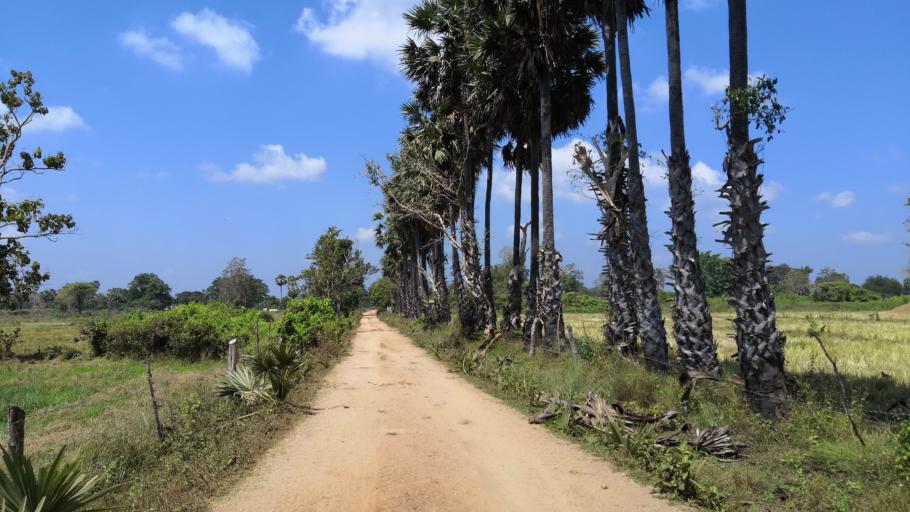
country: LK
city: Padaviya Divisional Secretariat
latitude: 8.9713
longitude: 80.6792
